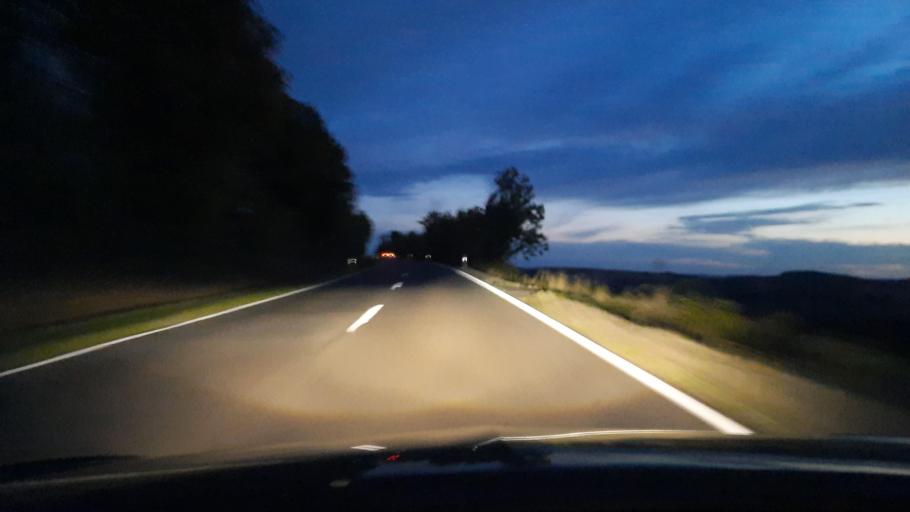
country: DE
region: Rheinland-Pfalz
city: Irsch
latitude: 49.7206
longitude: 6.7058
